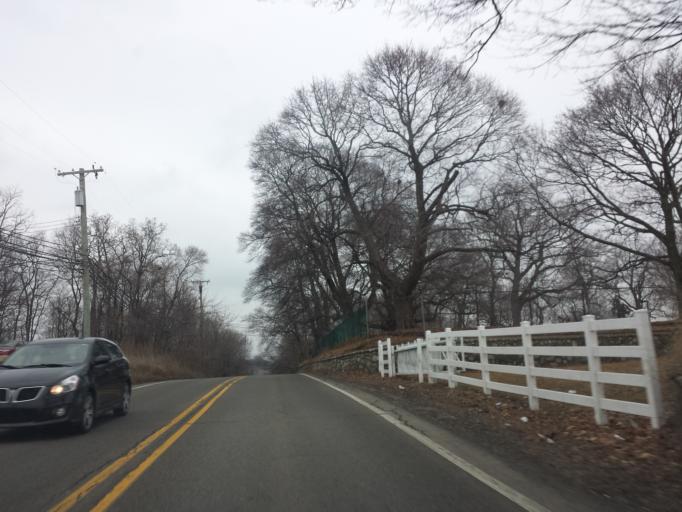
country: US
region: Michigan
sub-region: Oakland County
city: Auburn Hills
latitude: 42.6735
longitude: -83.1938
